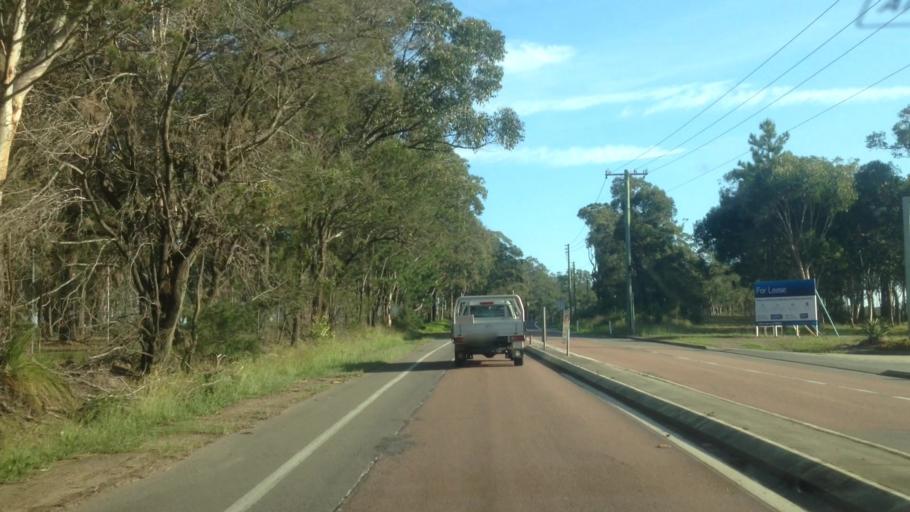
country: AU
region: New South Wales
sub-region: Lake Macquarie Shire
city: Dora Creek
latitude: -33.1164
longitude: 151.4783
